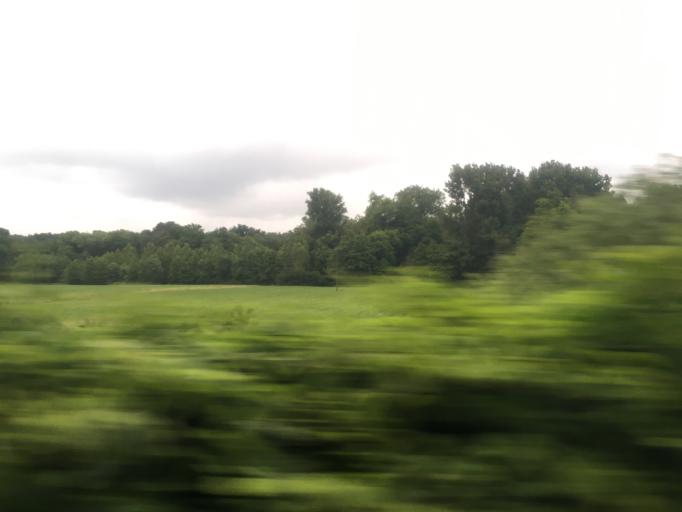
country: DE
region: North Rhine-Westphalia
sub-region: Regierungsbezirk Munster
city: Steinfurt
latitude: 52.1352
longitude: 7.3446
